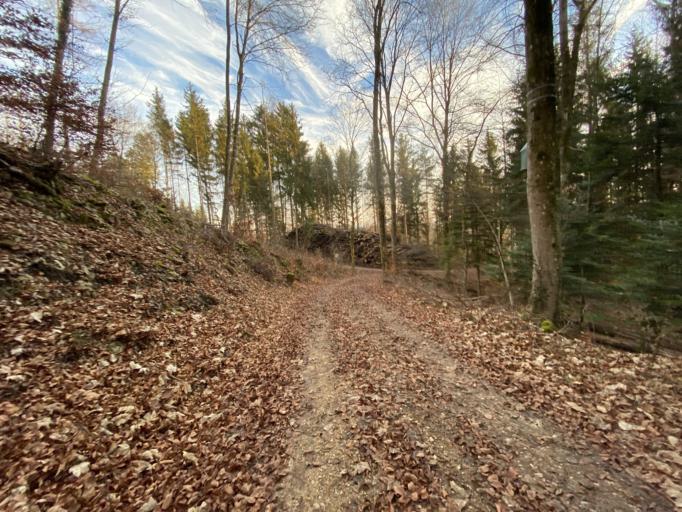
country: CH
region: Aargau
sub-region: Bezirk Laufenburg
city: Frick
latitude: 47.5108
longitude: 8.0387
